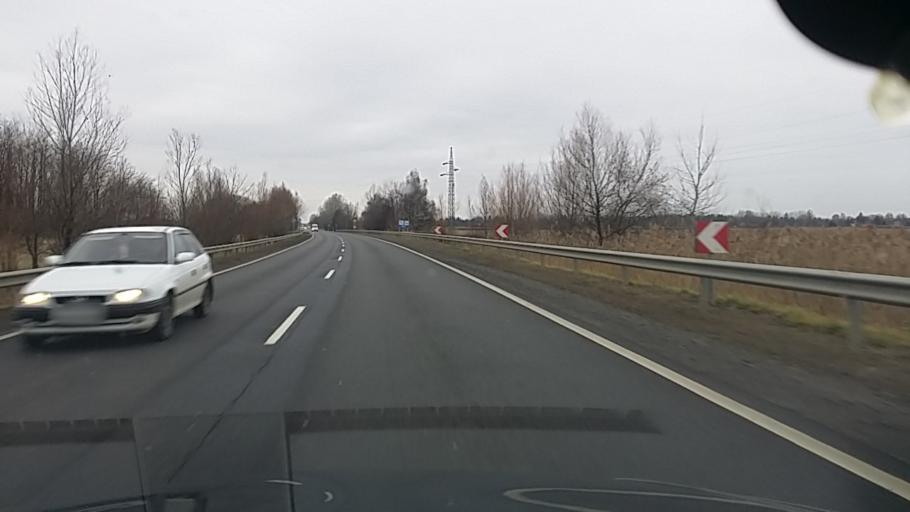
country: HU
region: Szabolcs-Szatmar-Bereg
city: Ujfeherto
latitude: 47.8755
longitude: 21.7058
